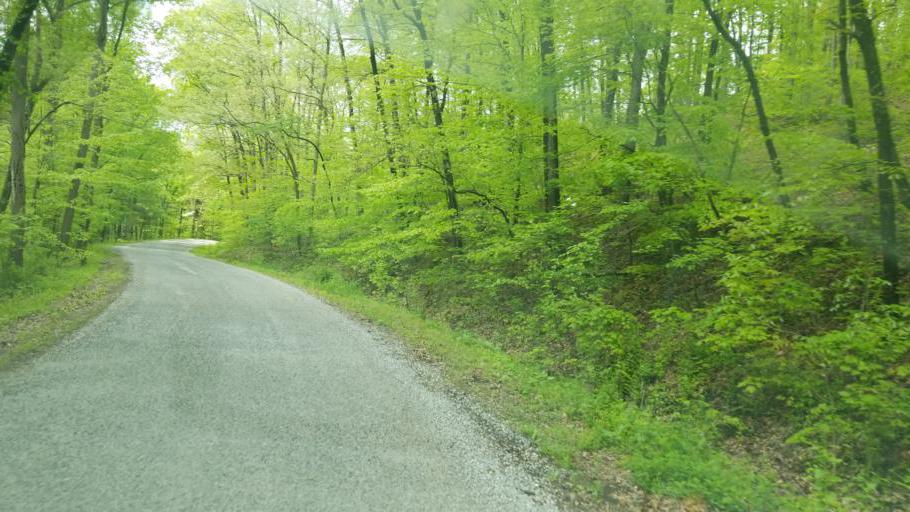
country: US
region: Ohio
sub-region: Tuscarawas County
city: Rockford
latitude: 40.4578
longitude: -81.2803
